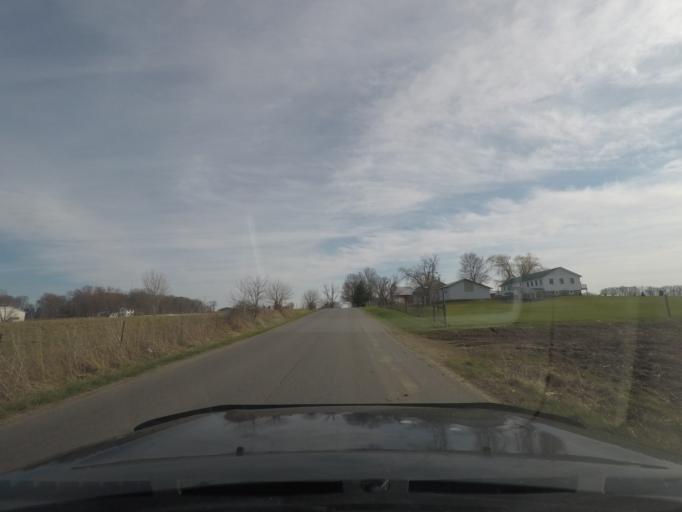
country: US
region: Indiana
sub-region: Elkhart County
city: Dunlap
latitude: 41.5479
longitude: -85.9248
